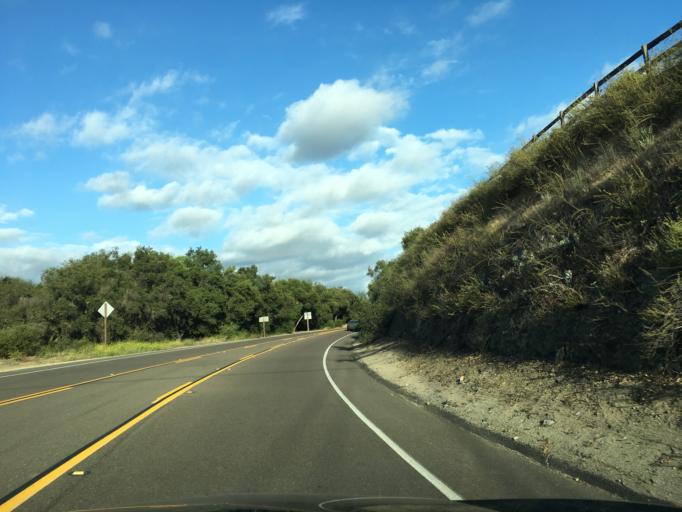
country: US
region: California
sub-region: San Diego County
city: Valley Center
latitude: 33.2560
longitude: -117.0680
